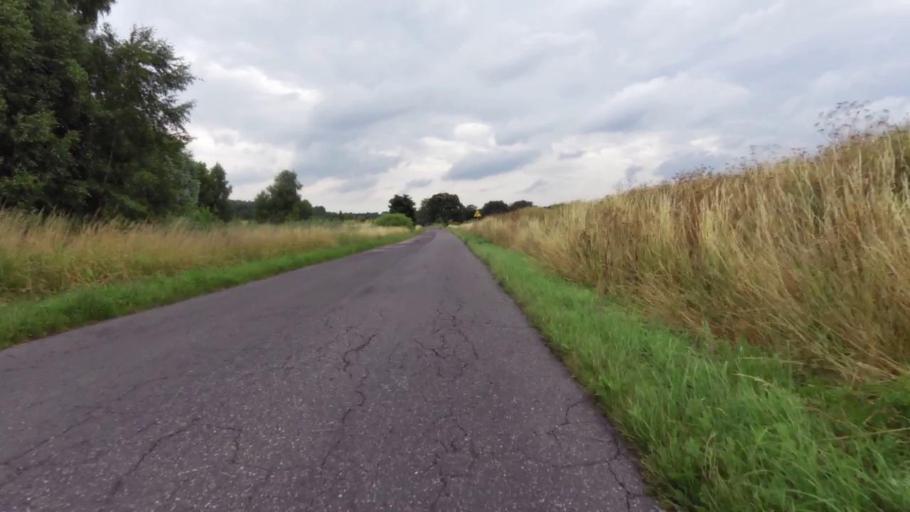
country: PL
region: West Pomeranian Voivodeship
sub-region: Powiat mysliborski
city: Mysliborz
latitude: 52.9594
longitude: 14.8832
